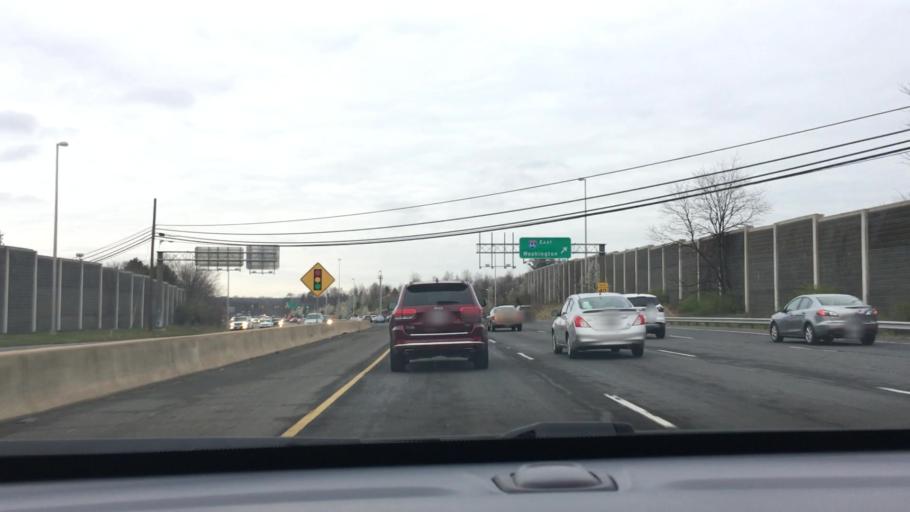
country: US
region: Virginia
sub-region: Fairfax County
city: Centreville
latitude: 38.8416
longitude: -77.4311
